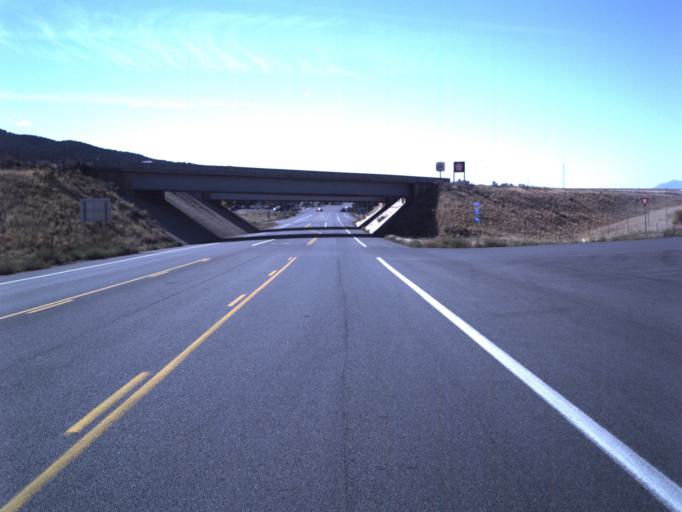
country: US
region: Utah
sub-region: Juab County
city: Nephi
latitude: 39.6827
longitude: -111.8387
